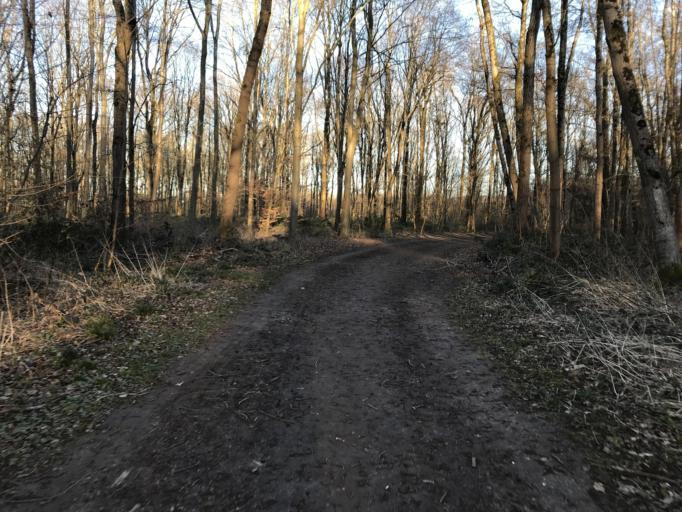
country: FR
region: Ile-de-France
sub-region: Departement de l'Essonne
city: Villebon-sur-Yvette
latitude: 48.7172
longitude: 2.2229
